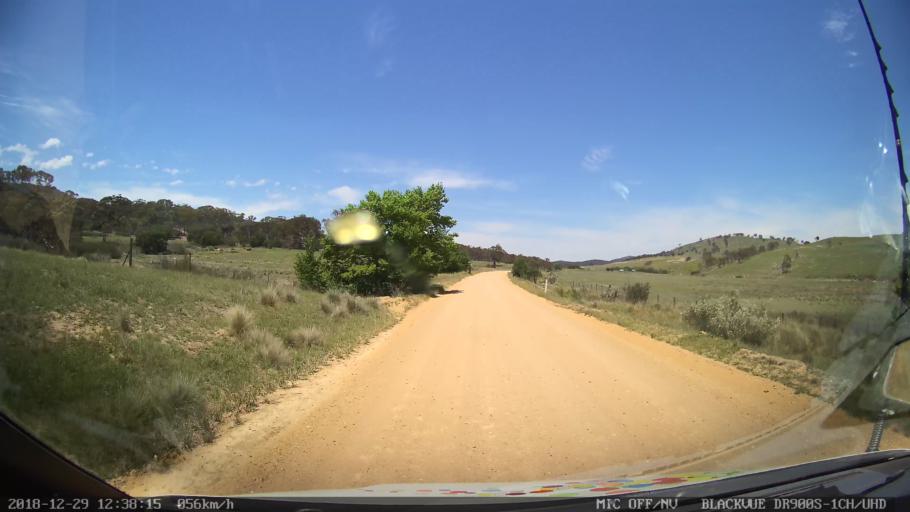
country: AU
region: Australian Capital Territory
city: Macarthur
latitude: -35.5871
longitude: 149.2293
